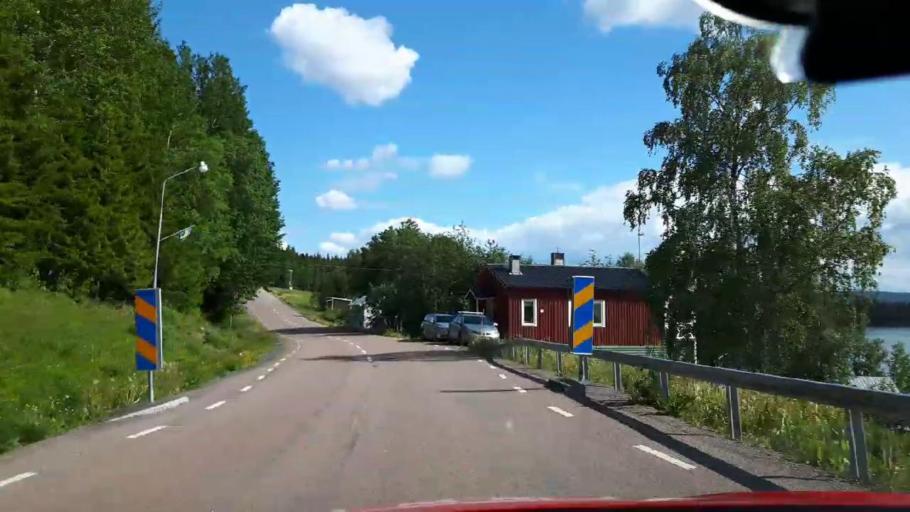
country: SE
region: Jaemtland
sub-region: Krokoms Kommun
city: Valla
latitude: 64.0664
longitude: 14.1420
